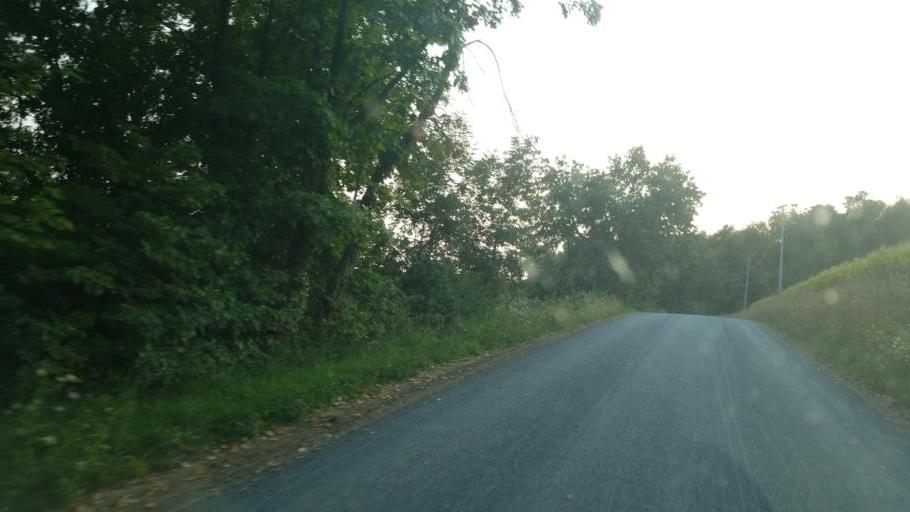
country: US
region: Ohio
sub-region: Knox County
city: Danville
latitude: 40.5360
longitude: -82.3473
